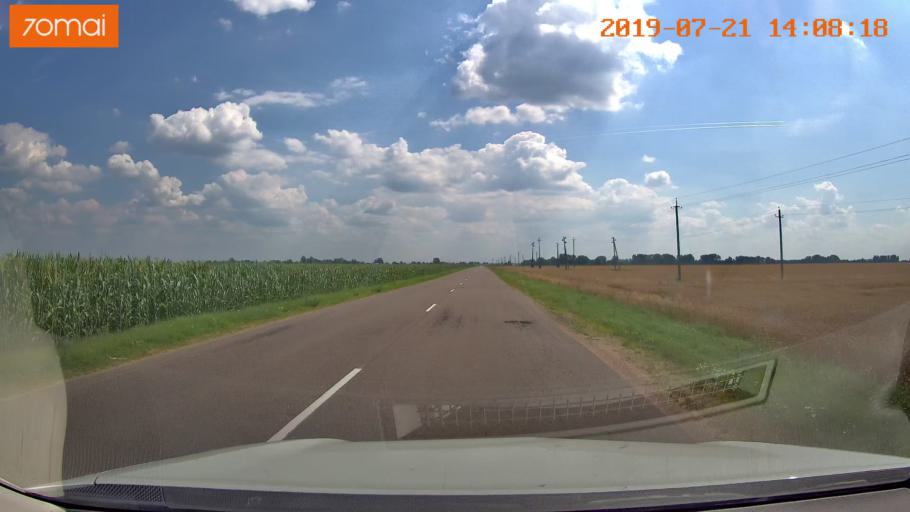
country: BY
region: Grodnenskaya
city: Lyubcha
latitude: 53.6741
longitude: 26.1245
